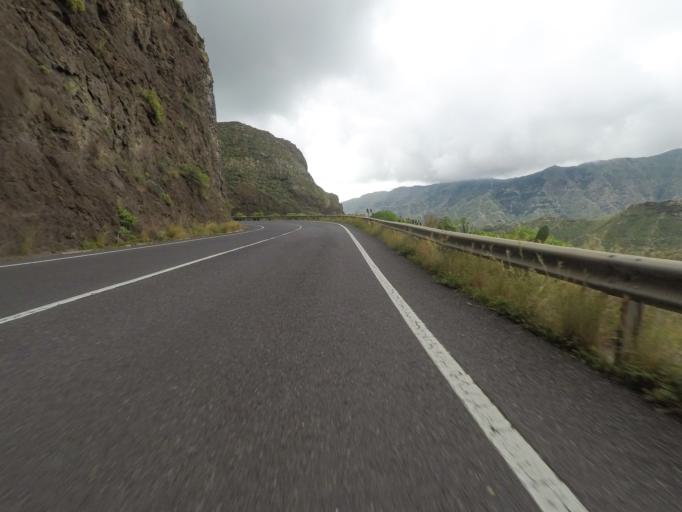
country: ES
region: Canary Islands
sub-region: Provincia de Santa Cruz de Tenerife
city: Hermigua
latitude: 28.1312
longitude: -17.1781
